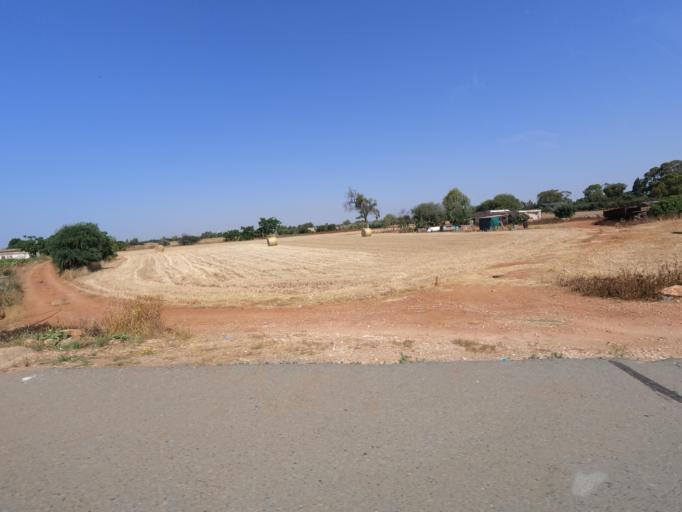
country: CY
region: Ammochostos
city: Liopetri
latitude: 34.9865
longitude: 33.9280
